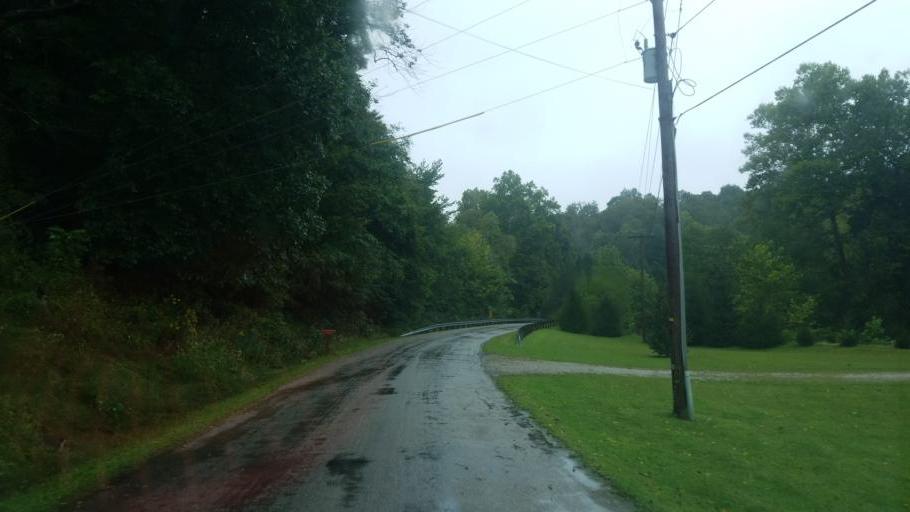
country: US
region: Ohio
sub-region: Adams County
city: Peebles
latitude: 38.8059
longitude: -83.2476
